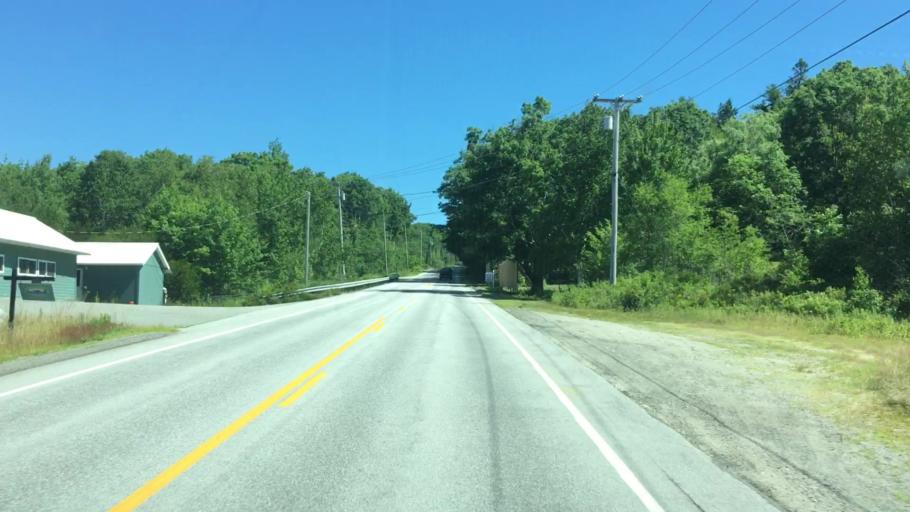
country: US
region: Maine
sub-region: Hancock County
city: Sedgwick
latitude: 44.3523
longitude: -68.6692
